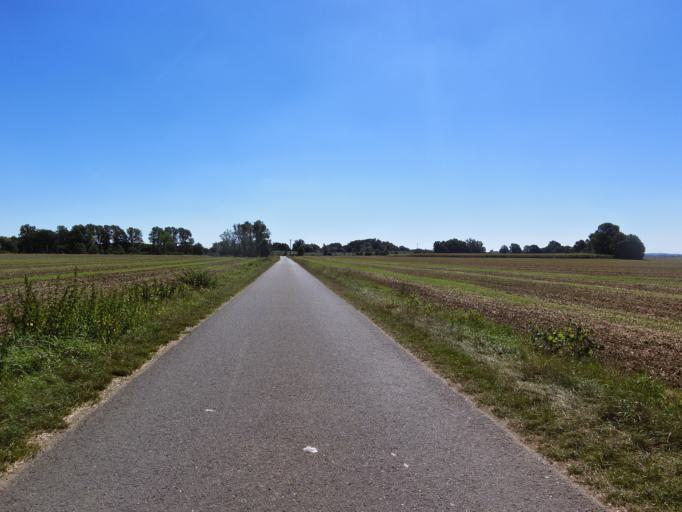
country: DE
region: Saxony-Anhalt
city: Pretzsch
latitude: 51.7429
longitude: 12.8276
